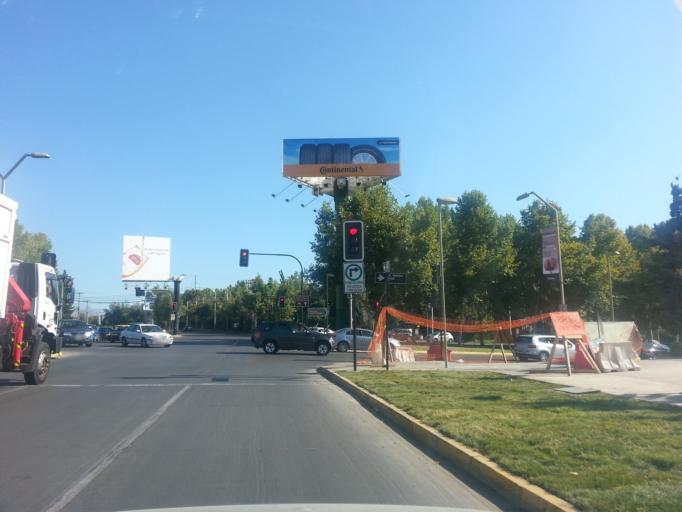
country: CL
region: Santiago Metropolitan
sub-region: Provincia de Santiago
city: Villa Presidente Frei, Nunoa, Santiago, Chile
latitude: -33.4284
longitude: -70.5392
